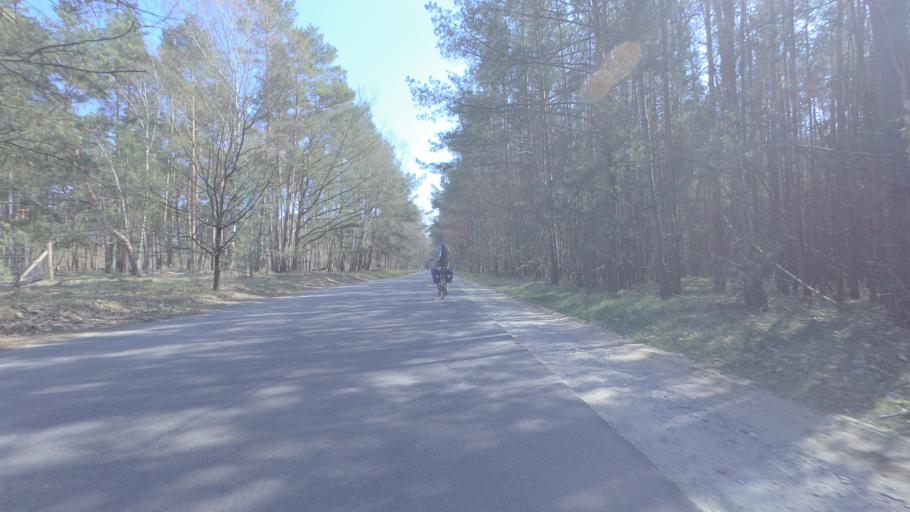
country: DE
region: Brandenburg
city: Bestensee
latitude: 52.2252
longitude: 13.5967
